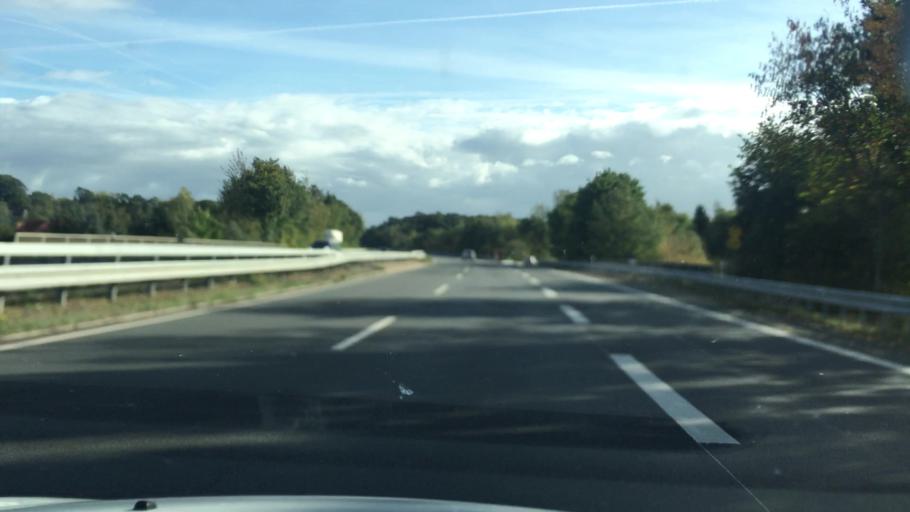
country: DE
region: Lower Saxony
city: Nienburg
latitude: 52.6230
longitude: 9.2426
